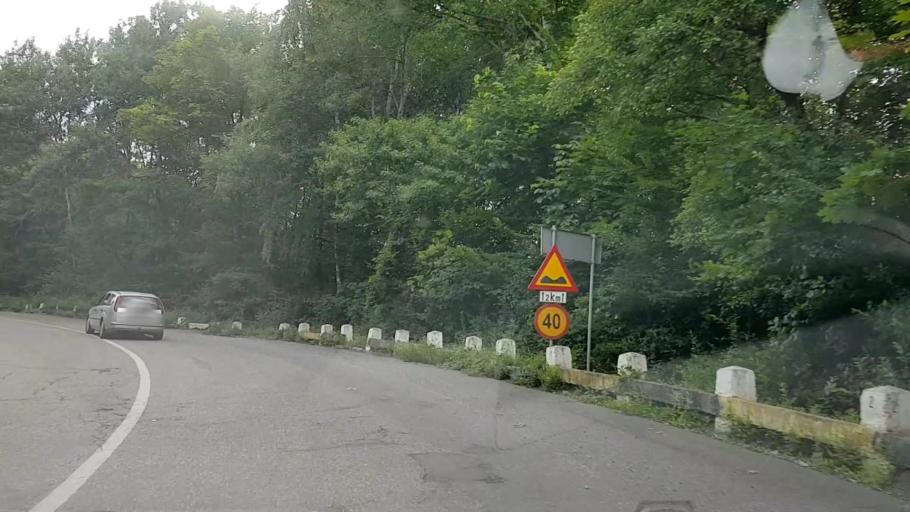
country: RO
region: Neamt
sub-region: Comuna Pangarati
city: Pangarati
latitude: 46.9459
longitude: 26.1269
